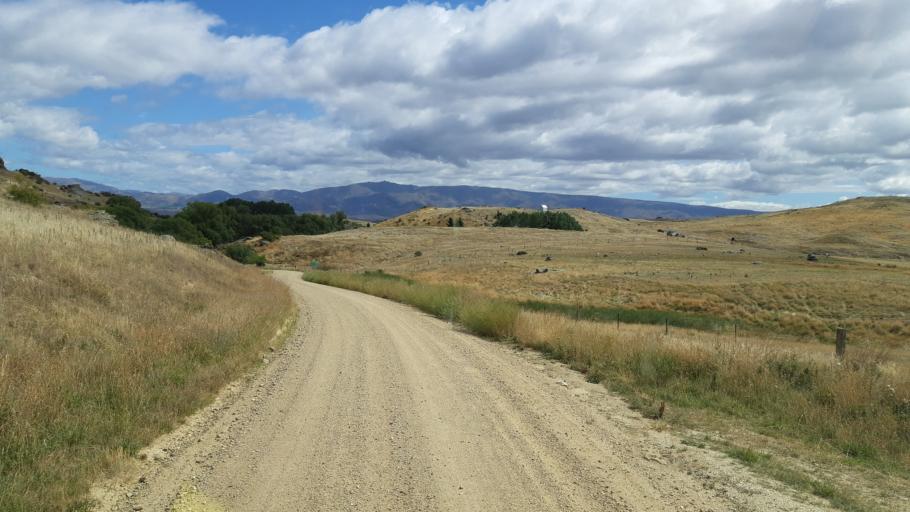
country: NZ
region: Otago
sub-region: Queenstown-Lakes District
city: Wanaka
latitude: -45.2128
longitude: 169.5575
